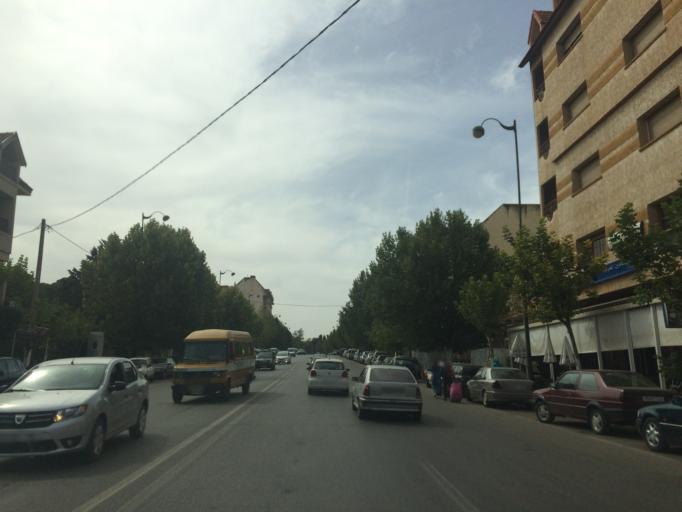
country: MA
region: Meknes-Tafilalet
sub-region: El-Hajeb
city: El Hajeb
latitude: 33.6857
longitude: -5.3709
